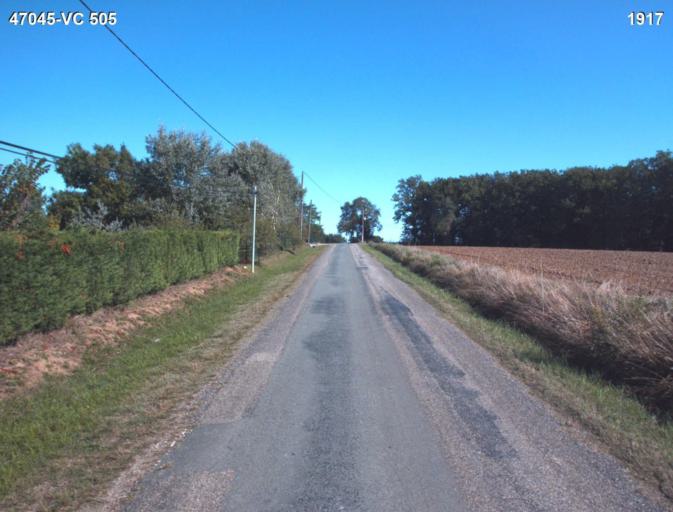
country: FR
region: Aquitaine
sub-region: Departement du Lot-et-Garonne
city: Nerac
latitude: 44.1475
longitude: 0.4153
